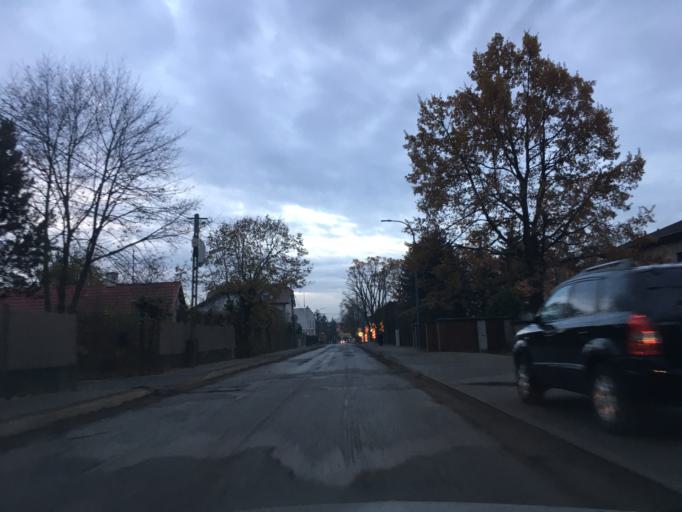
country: PL
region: Masovian Voivodeship
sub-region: Powiat piaseczynski
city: Piaseczno
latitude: 52.0521
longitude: 20.9868
